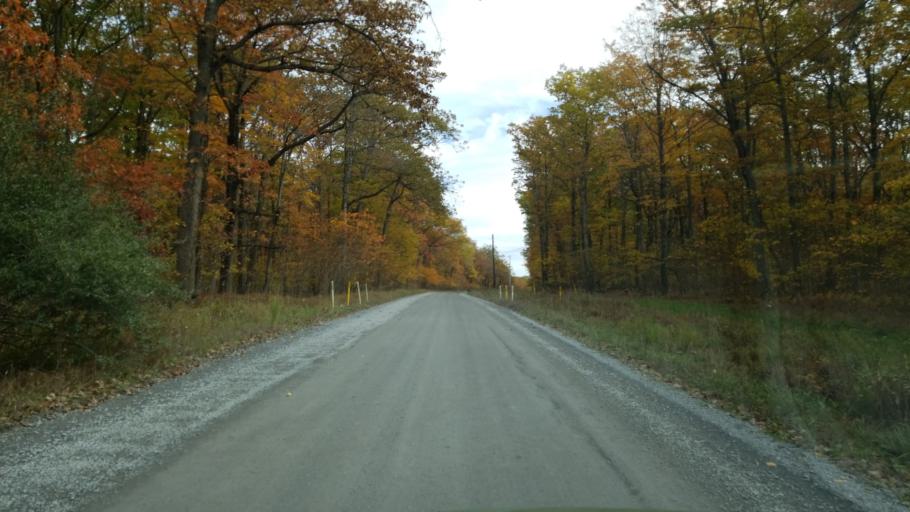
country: US
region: Pennsylvania
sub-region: Clearfield County
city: Clearfield
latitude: 41.1430
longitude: -78.4975
